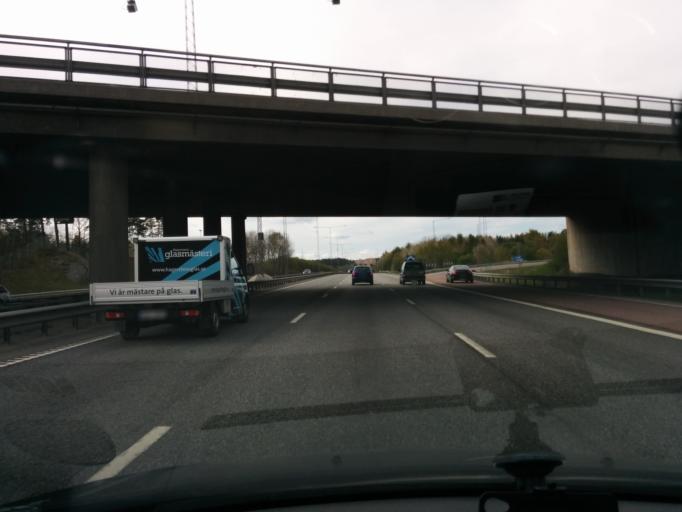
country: SE
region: Stockholm
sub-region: Botkyrka Kommun
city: Fittja
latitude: 59.2524
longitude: 17.8569
